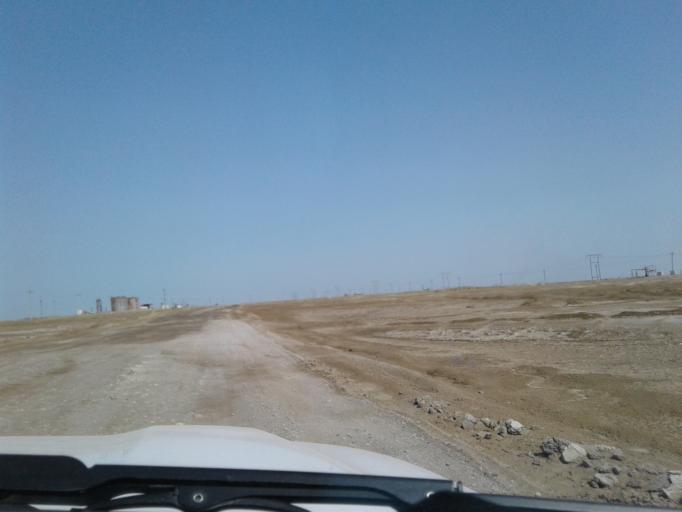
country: IR
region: Golestan
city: Gomishan
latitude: 37.7640
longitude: 53.9234
